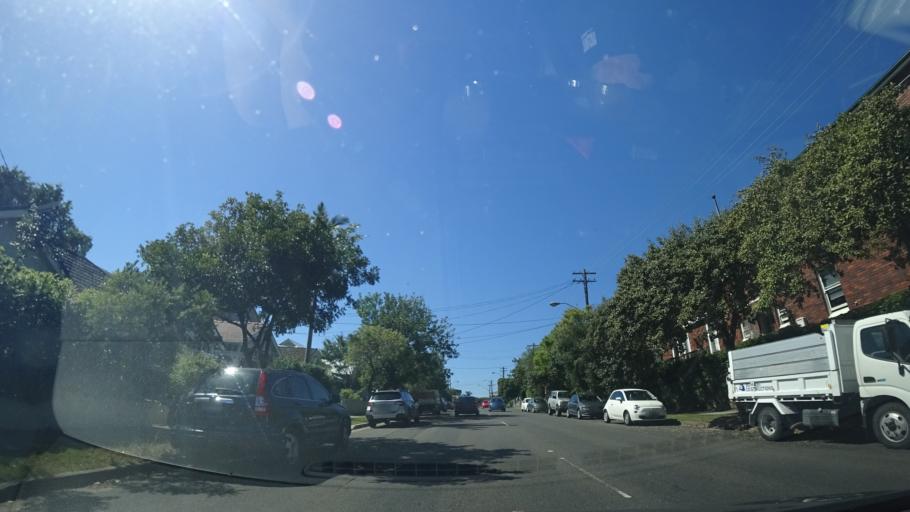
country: AU
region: New South Wales
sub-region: Randwick
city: Randwick
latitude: -33.9071
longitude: 151.2471
